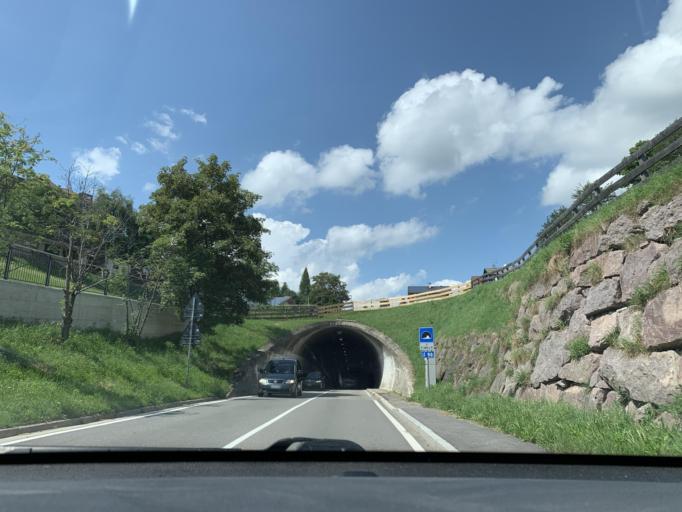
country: IT
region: Trentino-Alto Adige
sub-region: Bolzano
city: Avelengo
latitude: 46.6449
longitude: 11.2255
